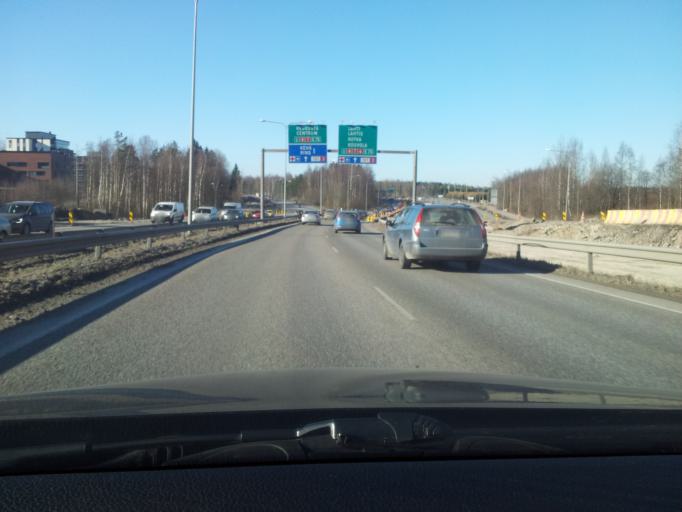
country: FI
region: Uusimaa
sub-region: Helsinki
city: Vantaa
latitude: 60.2317
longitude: 25.0509
